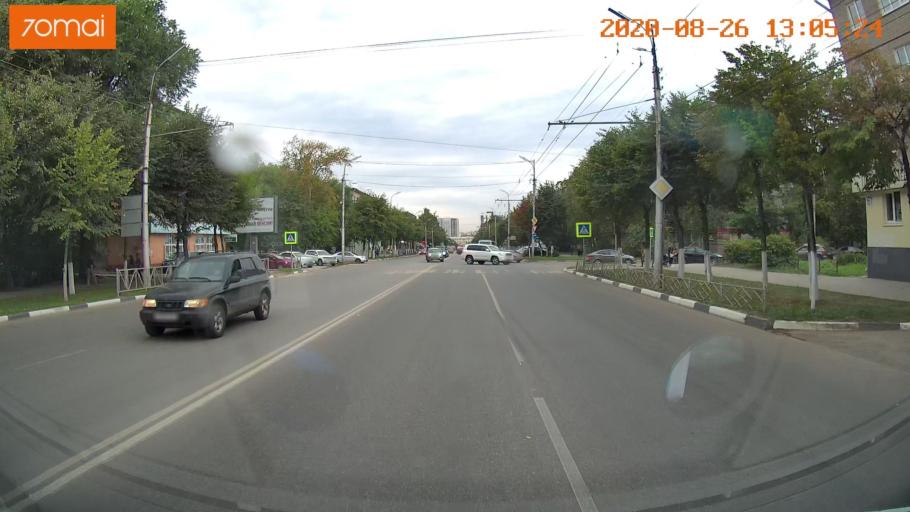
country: RU
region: Rjazan
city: Ryazan'
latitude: 54.6196
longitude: 39.7254
